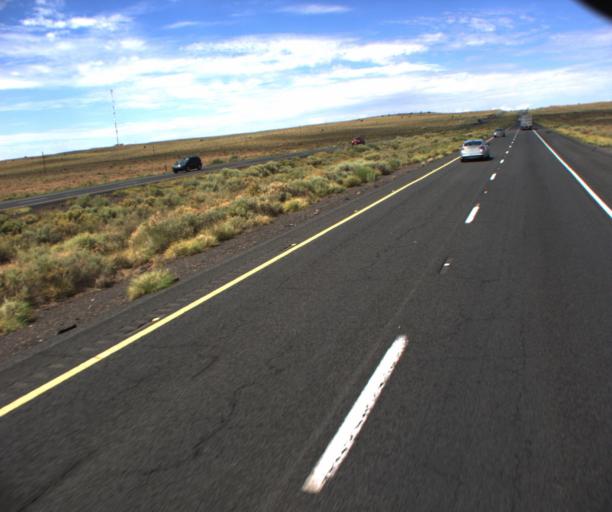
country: US
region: Arizona
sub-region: Apache County
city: Houck
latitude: 35.1101
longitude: -109.5945
